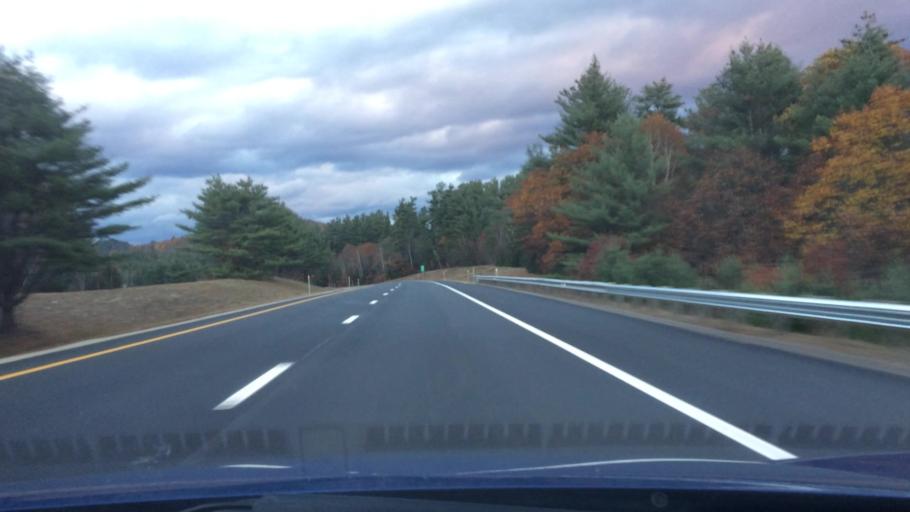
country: US
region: New Hampshire
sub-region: Grafton County
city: Thornton
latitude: 43.9282
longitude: -71.6873
